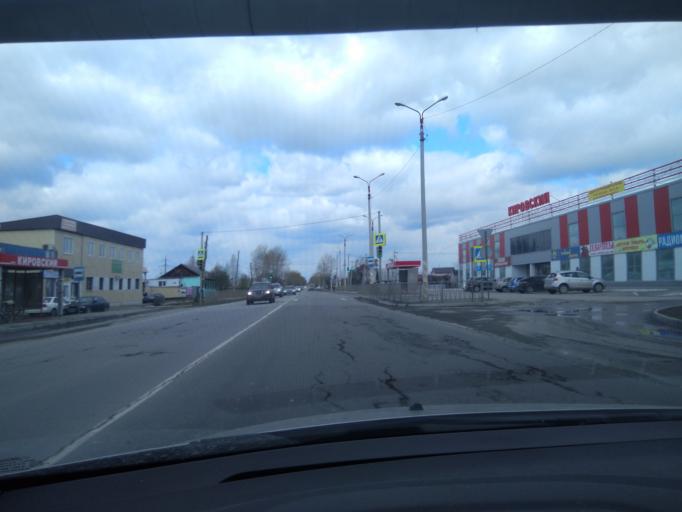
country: RU
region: Sverdlovsk
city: Sredneuralsk
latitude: 56.9890
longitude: 60.4965
